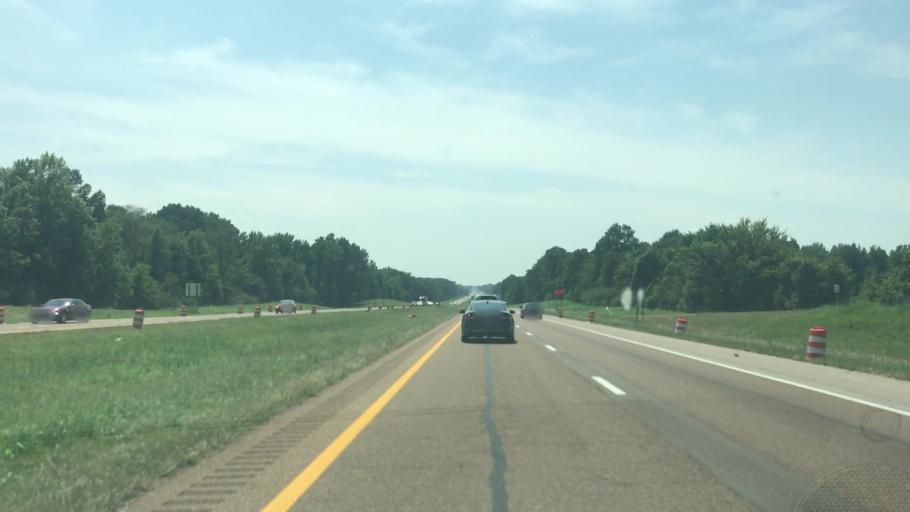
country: US
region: Tennessee
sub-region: Tipton County
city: Mason
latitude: 35.3483
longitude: -89.5200
